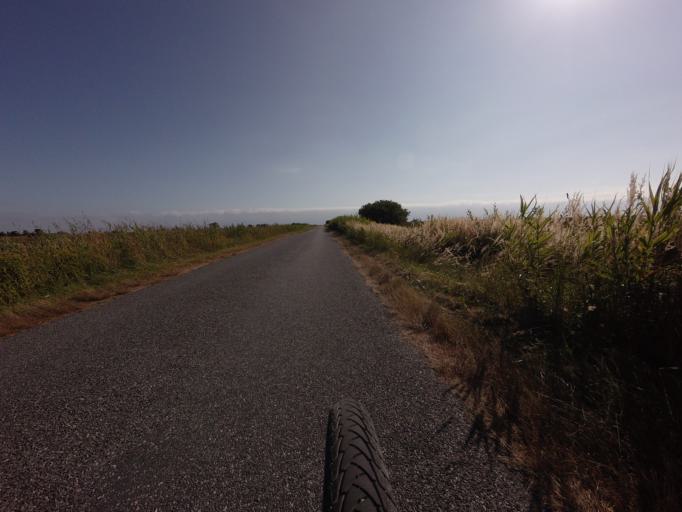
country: DK
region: North Denmark
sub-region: Laeso Kommune
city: Byrum
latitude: 57.2563
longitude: 10.8836
